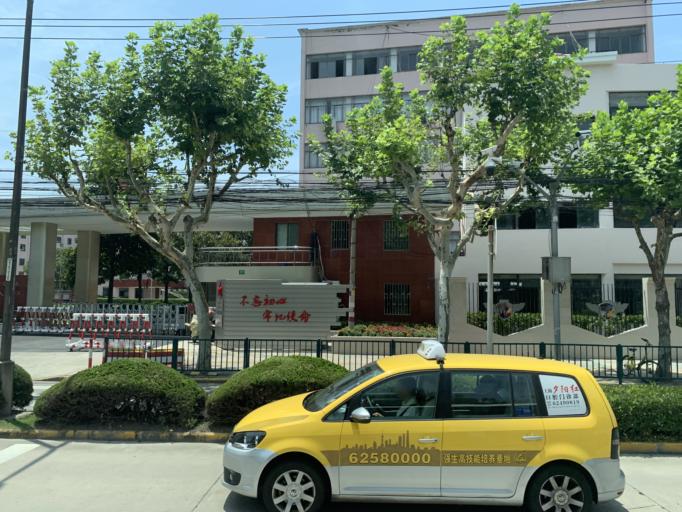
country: CN
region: Shanghai Shi
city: Pudong
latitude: 31.2399
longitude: 121.5267
